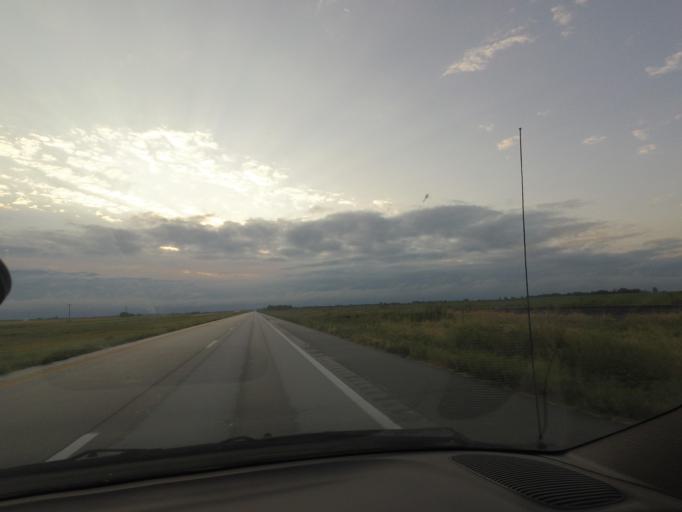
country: US
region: Missouri
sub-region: Shelby County
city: Shelbina
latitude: 39.7077
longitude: -92.1002
